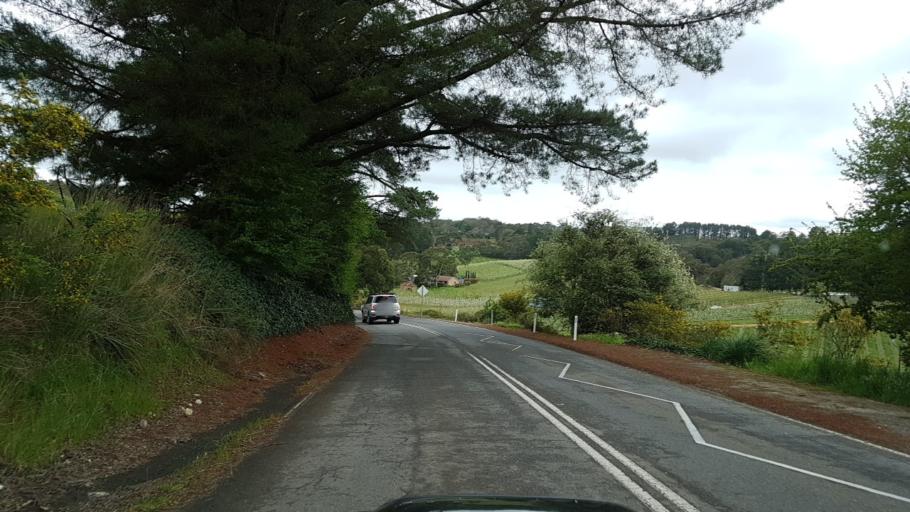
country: AU
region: South Australia
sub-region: Adelaide Hills
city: Lobethal
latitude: -34.9221
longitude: 138.8246
